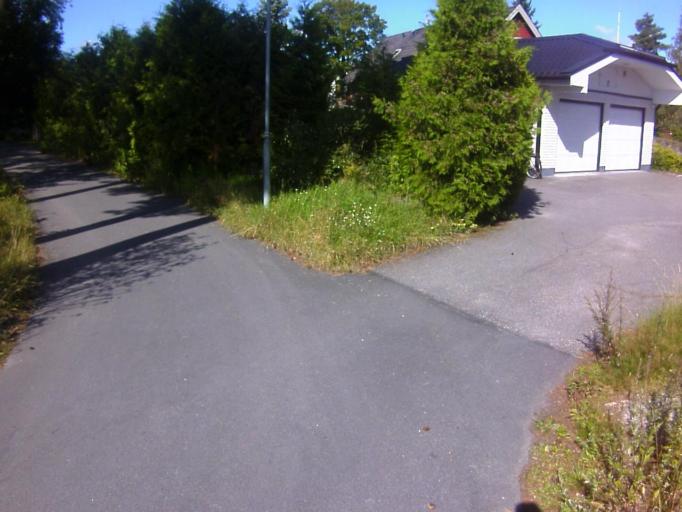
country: SE
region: Soedermanland
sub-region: Eskilstuna Kommun
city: Hallbybrunn
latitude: 59.3730
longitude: 16.4443
